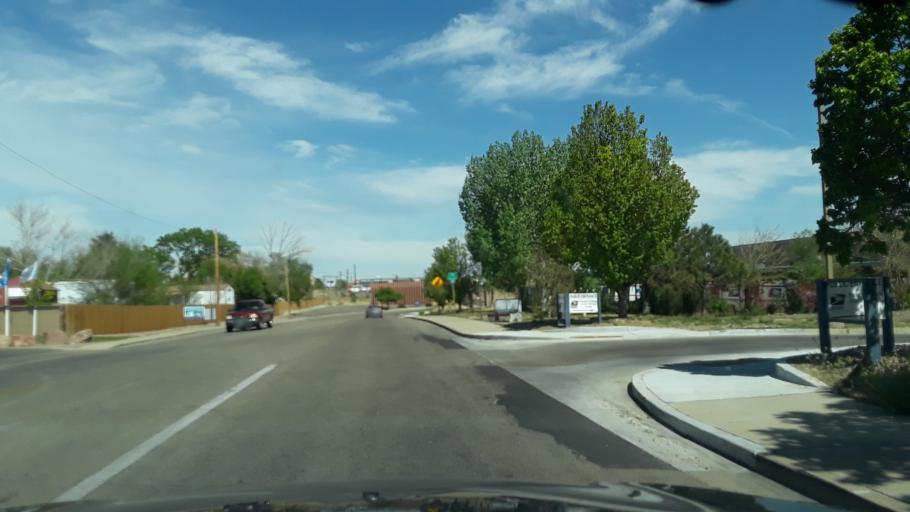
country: US
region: Colorado
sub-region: Pueblo County
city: Pueblo
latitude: 38.3125
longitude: -104.6206
